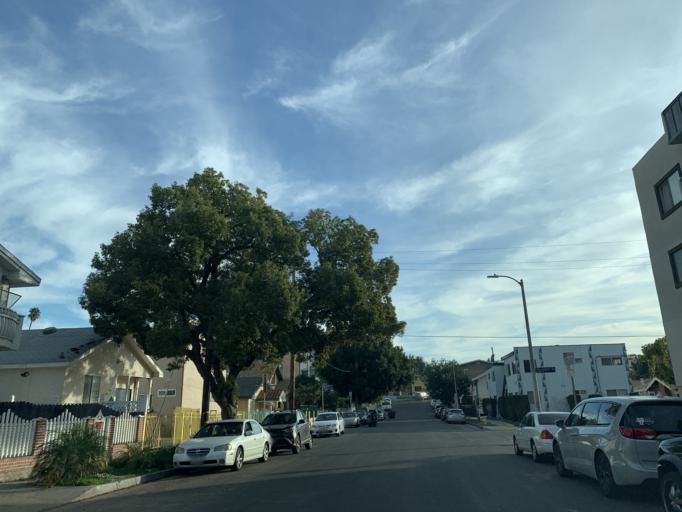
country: US
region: California
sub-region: Los Angeles County
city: Hollywood
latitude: 34.0503
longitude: -118.3074
